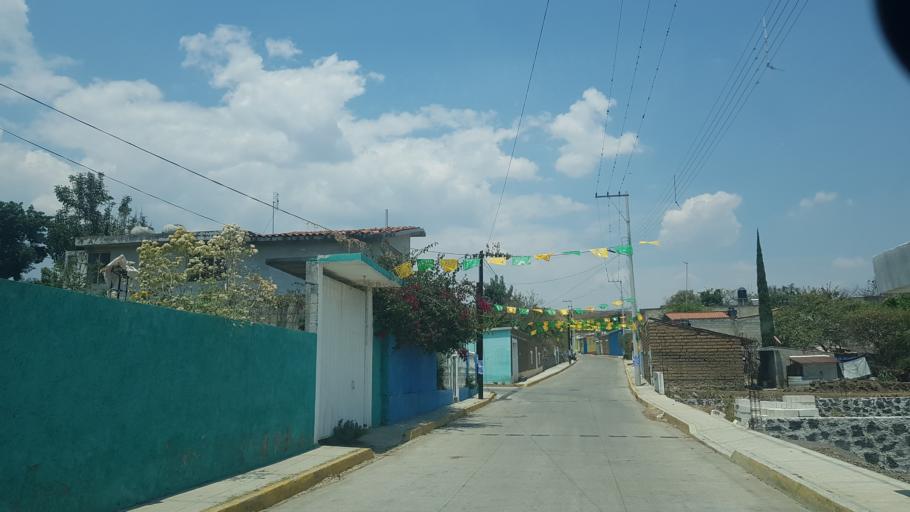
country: MX
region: Puebla
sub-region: Atzitzihuacan
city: Santiago Atzitzihuacan
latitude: 18.8261
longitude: -98.5816
